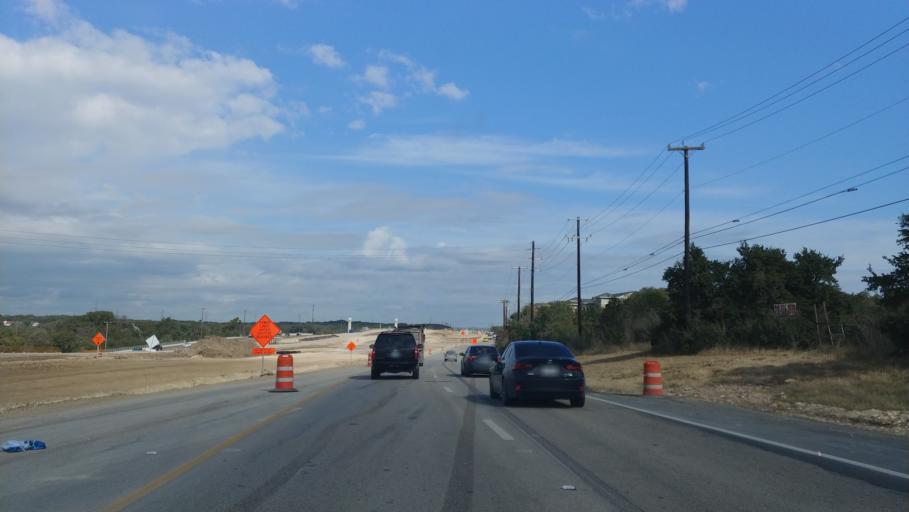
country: US
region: Texas
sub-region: Bexar County
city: Leon Valley
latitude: 29.4588
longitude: -98.7111
